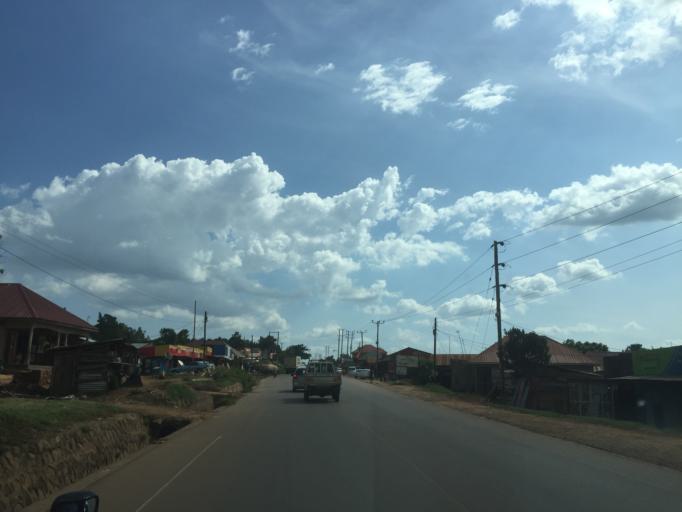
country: UG
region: Central Region
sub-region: Wakiso District
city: Wakiso
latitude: 0.5104
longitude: 32.5256
